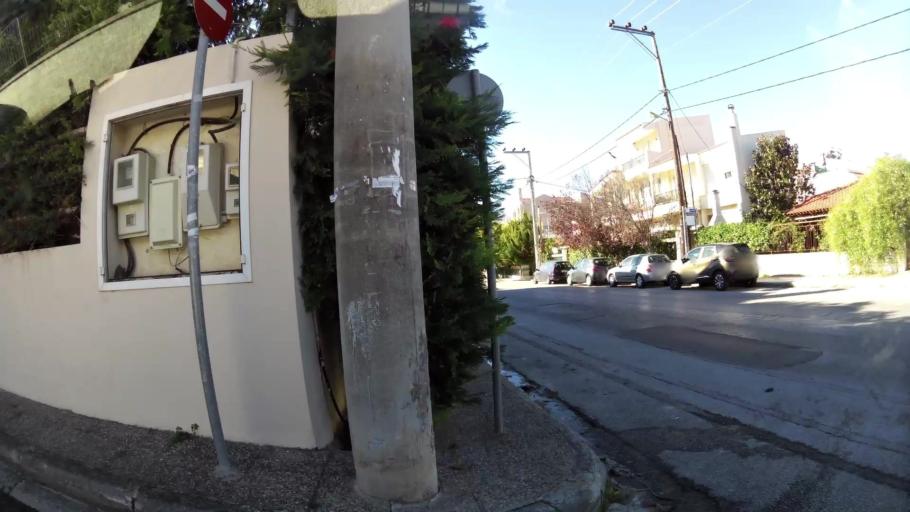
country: GR
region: Attica
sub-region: Nomarchia Anatolikis Attikis
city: Gerakas
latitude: 38.0179
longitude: 23.8543
